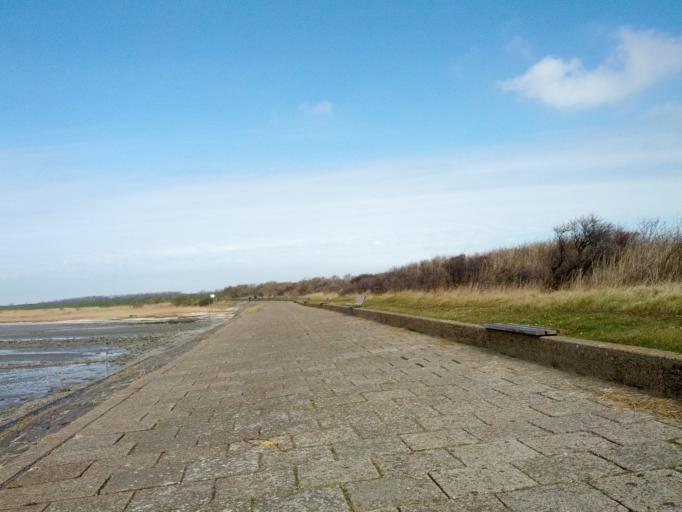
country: DE
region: Lower Saxony
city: Langeoog
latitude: 53.7232
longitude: 7.4914
